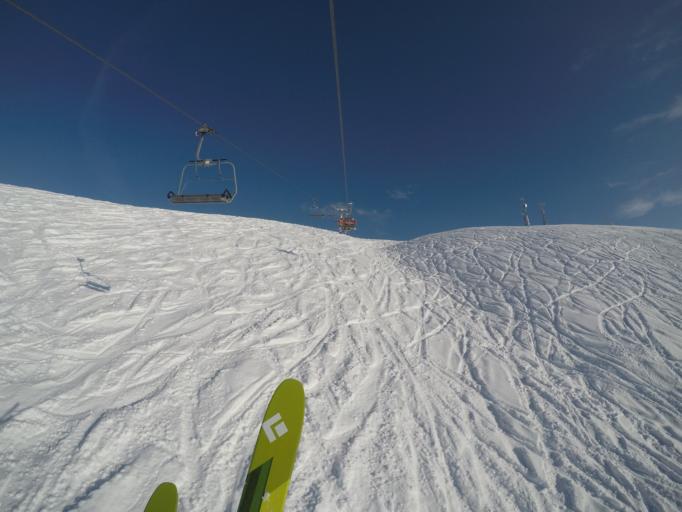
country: GE
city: Gudauri
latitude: 42.4874
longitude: 44.4976
